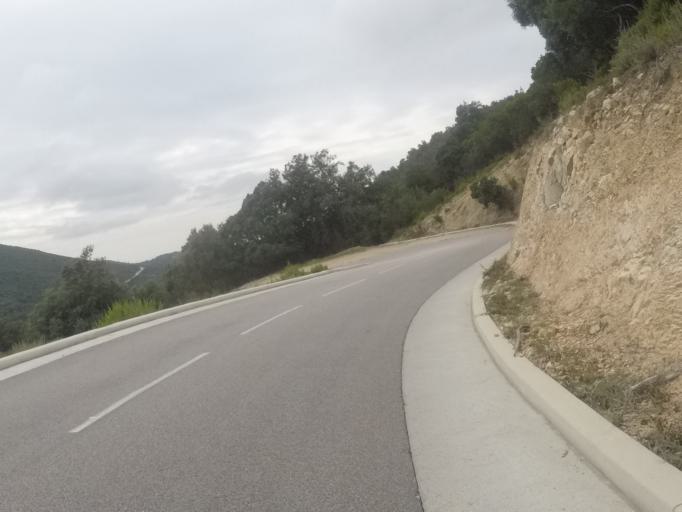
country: FR
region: Corsica
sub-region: Departement de la Corse-du-Sud
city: Pietrosella
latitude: 41.7918
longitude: 8.8231
